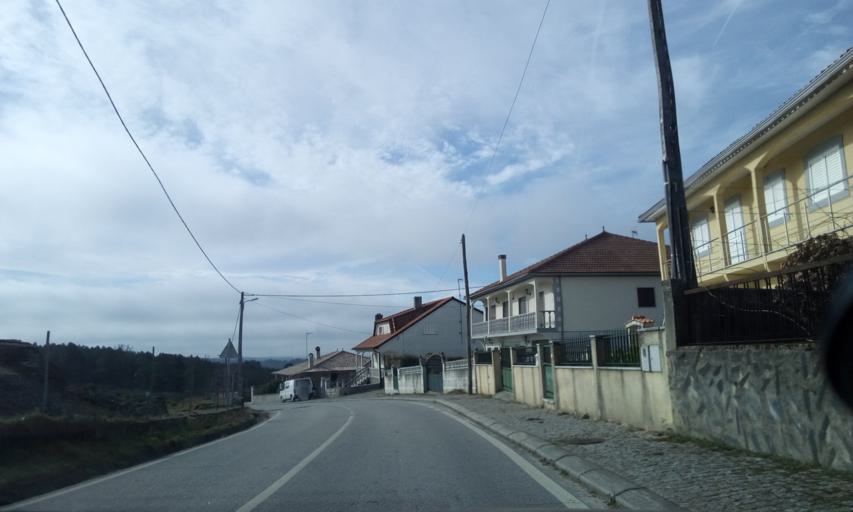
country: PT
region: Guarda
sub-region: Aguiar da Beira
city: Aguiar da Beira
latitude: 40.7806
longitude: -7.5182
